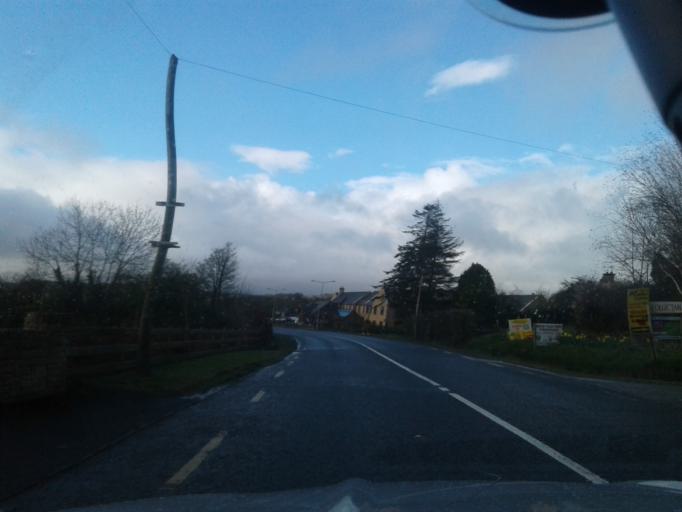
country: IE
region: Ulster
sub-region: County Donegal
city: Ramelton
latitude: 54.9872
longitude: -7.6683
